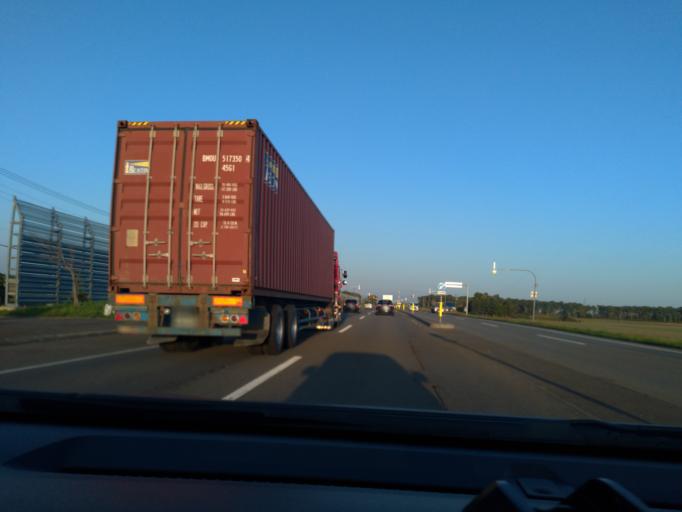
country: JP
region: Hokkaido
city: Tobetsu
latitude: 43.1801
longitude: 141.4730
